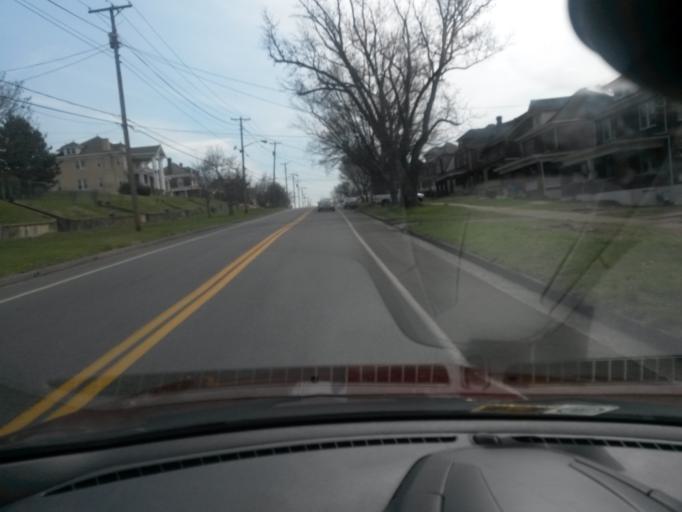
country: US
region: Virginia
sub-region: City of Roanoke
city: Roanoke
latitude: 37.2743
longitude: -79.9723
